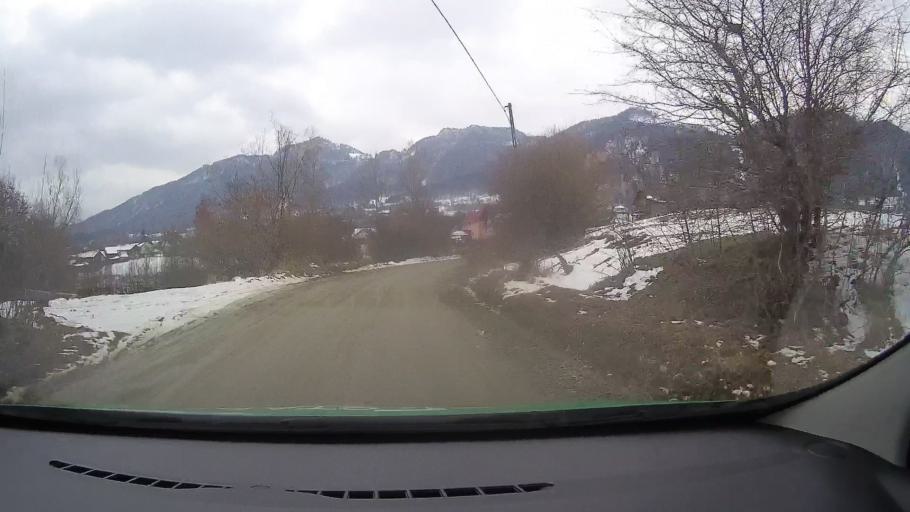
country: RO
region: Brasov
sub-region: Comuna Zarnesti
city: Zarnesti
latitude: 45.5457
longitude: 25.3224
